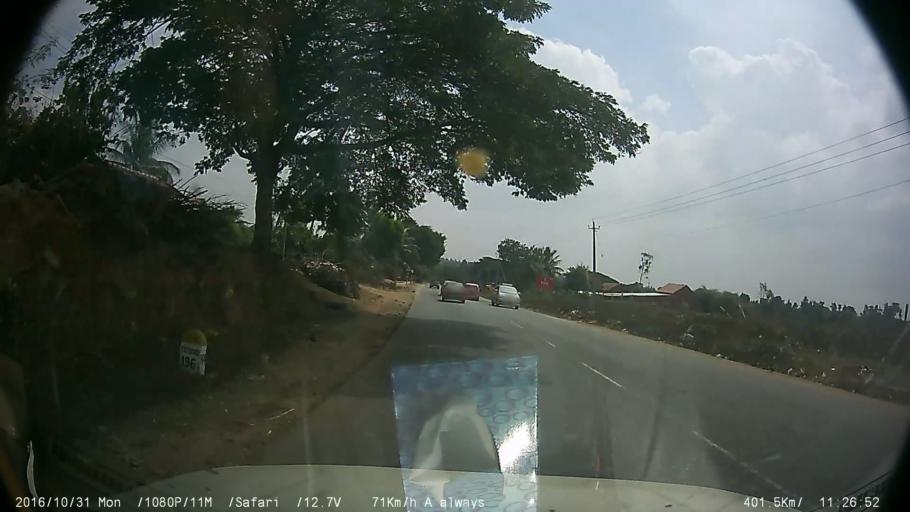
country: IN
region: Karnataka
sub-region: Mysore
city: Hunsur
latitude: 12.3309
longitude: 76.2053
